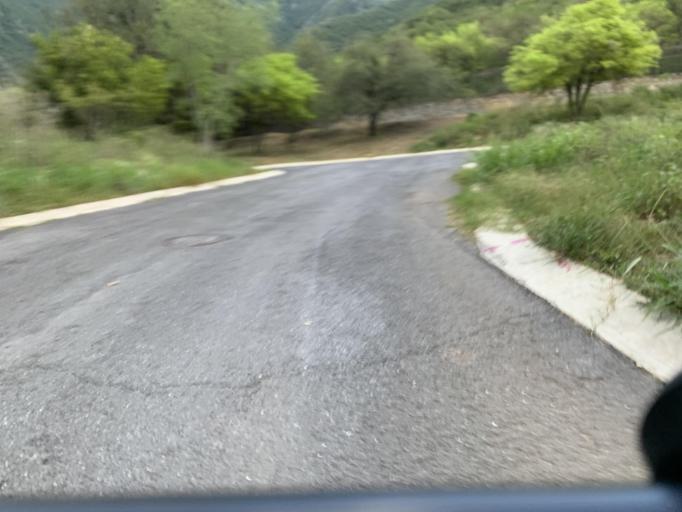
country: MX
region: Nuevo Leon
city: Santiago
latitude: 25.5080
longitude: -100.1786
